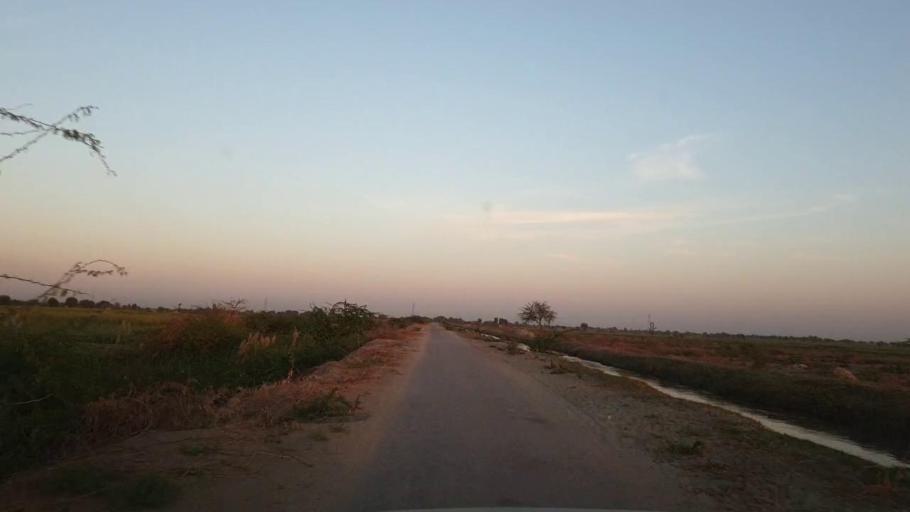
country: PK
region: Sindh
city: Kunri
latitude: 25.1476
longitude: 69.4345
